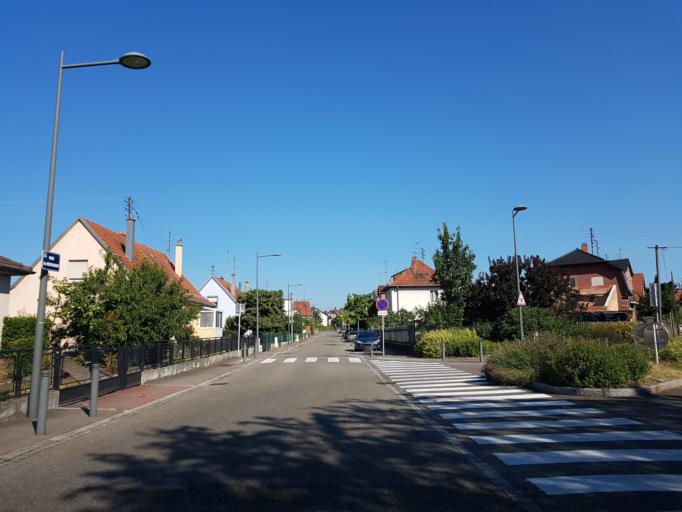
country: FR
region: Alsace
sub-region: Departement du Haut-Rhin
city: Riedisheim
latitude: 47.7627
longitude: 7.3631
